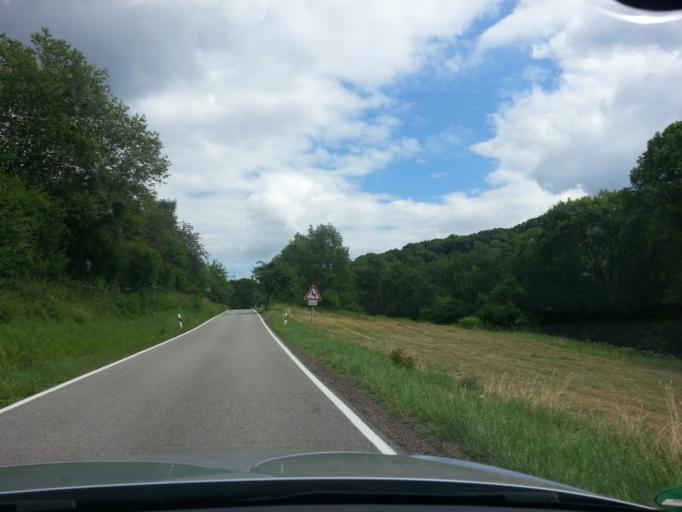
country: DE
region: Saarland
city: Beckingen
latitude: 49.4378
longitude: 6.6881
